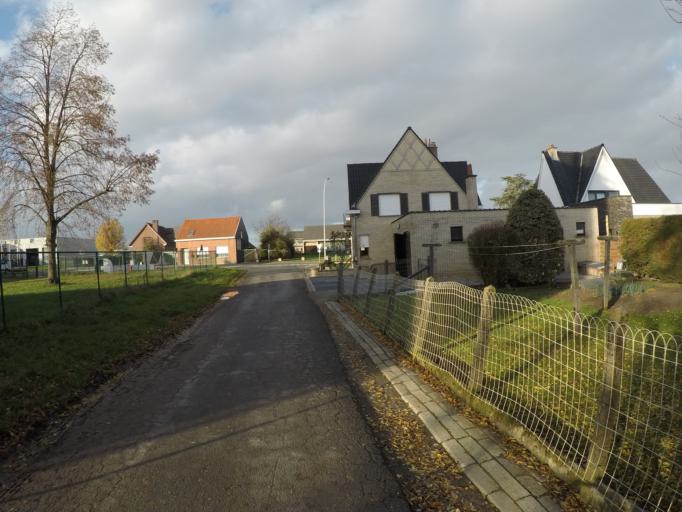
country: BE
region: Flanders
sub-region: Provincie Vlaams-Brabant
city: Opwijk
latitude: 50.9538
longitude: 4.1765
